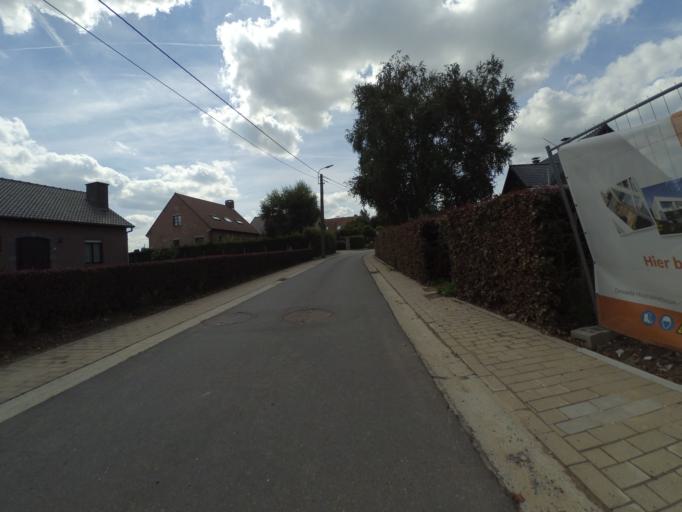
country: BE
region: Flanders
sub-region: Provincie Oost-Vlaanderen
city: Zottegem
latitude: 50.8466
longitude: 3.7482
